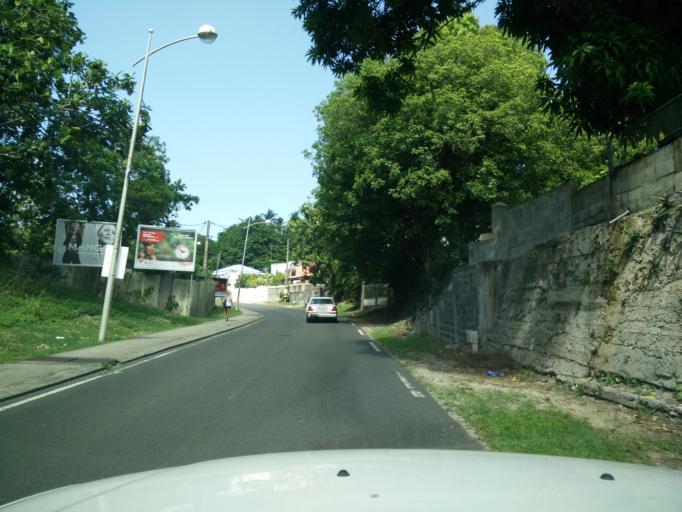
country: GP
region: Guadeloupe
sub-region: Guadeloupe
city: Le Gosier
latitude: 16.2102
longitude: -61.4798
